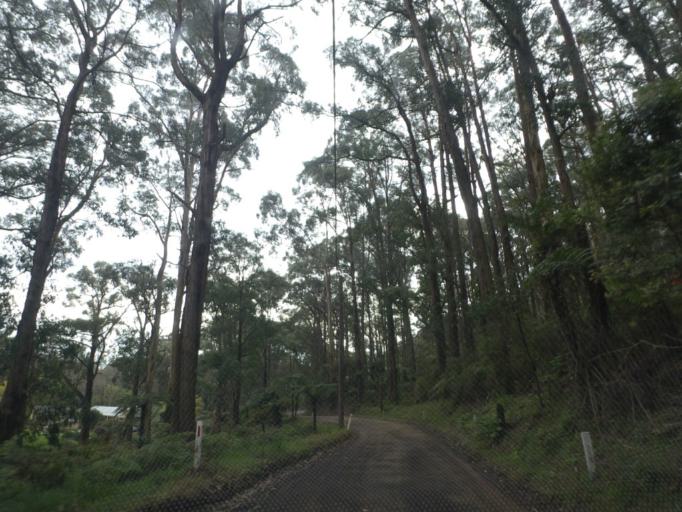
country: AU
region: Victoria
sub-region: Yarra Ranges
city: Olinda
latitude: -37.8570
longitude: 145.3446
